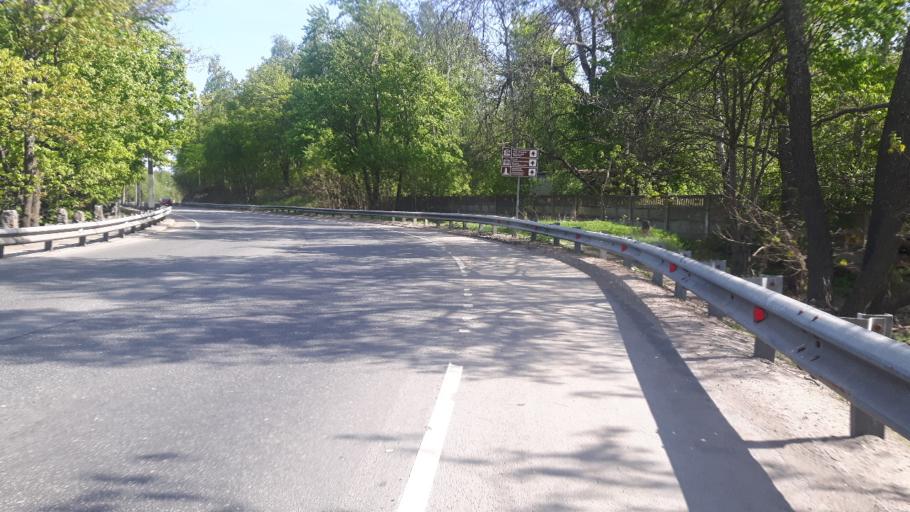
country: RU
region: Leningrad
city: Vyborg
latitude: 60.7247
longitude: 28.7088
